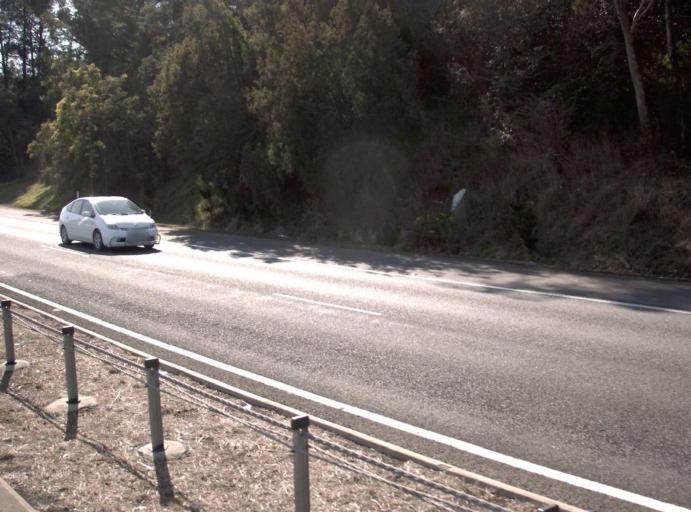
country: AU
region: Tasmania
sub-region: Launceston
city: Newnham
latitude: -41.4048
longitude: 147.1216
